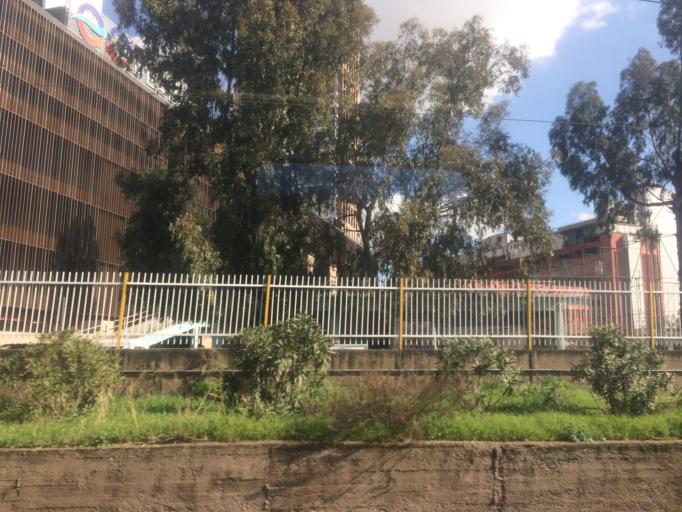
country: TR
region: Izmir
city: Izmir
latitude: 38.4470
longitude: 27.1732
